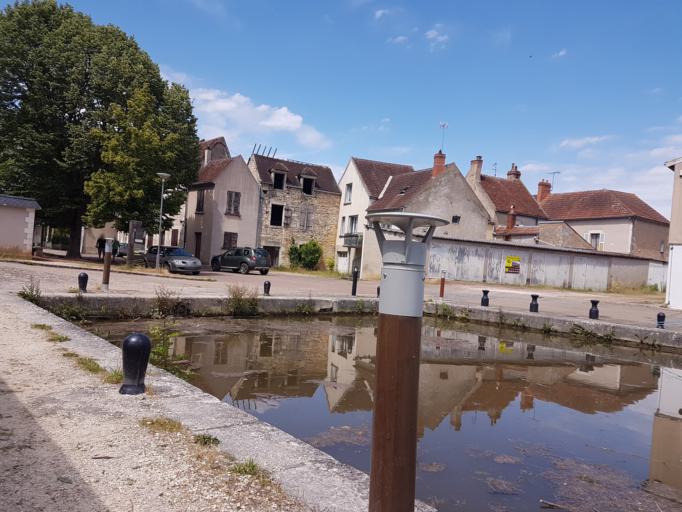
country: FR
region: Bourgogne
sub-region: Departement de la Nievre
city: Clamecy
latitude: 47.4577
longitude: 3.5220
